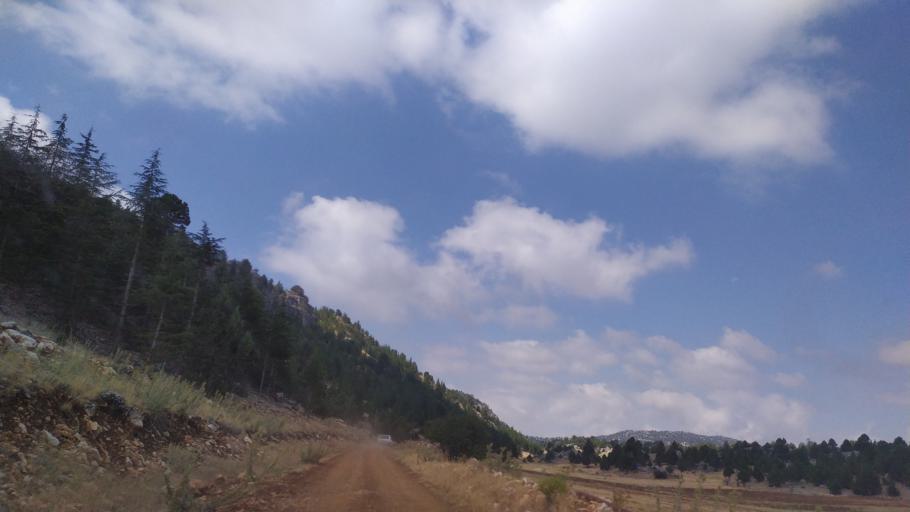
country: TR
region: Mersin
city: Kirobasi
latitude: 36.6219
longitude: 33.8460
